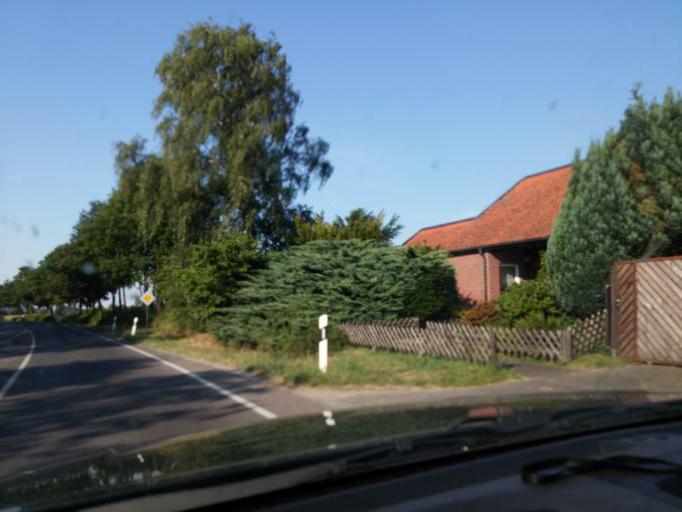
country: DE
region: North Rhine-Westphalia
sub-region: Regierungsbezirk Dusseldorf
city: Viersen
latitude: 51.2029
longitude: 6.3463
